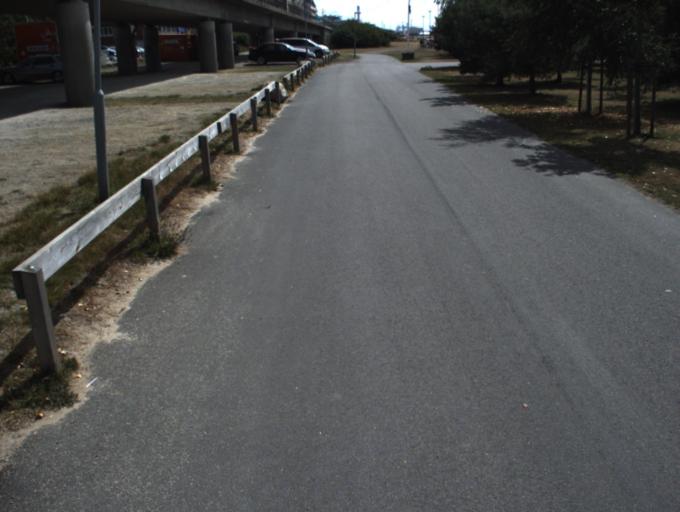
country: SE
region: Skane
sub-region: Helsingborg
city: Helsingborg
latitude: 56.0565
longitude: 12.6827
